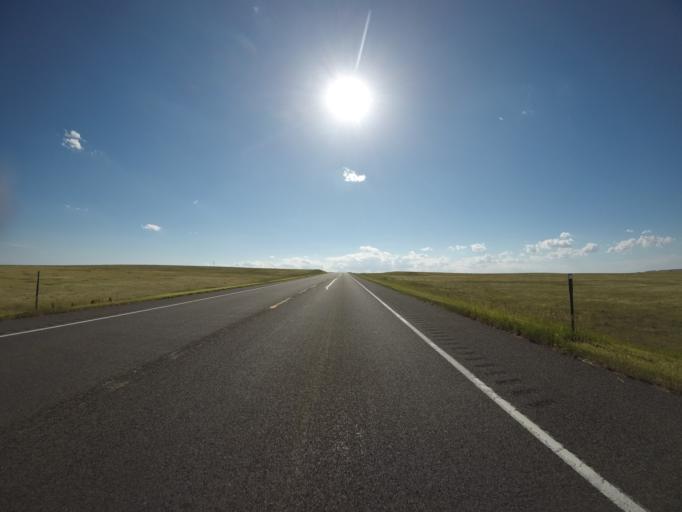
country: US
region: Colorado
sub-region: Morgan County
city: Brush
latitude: 40.6108
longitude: -103.5893
